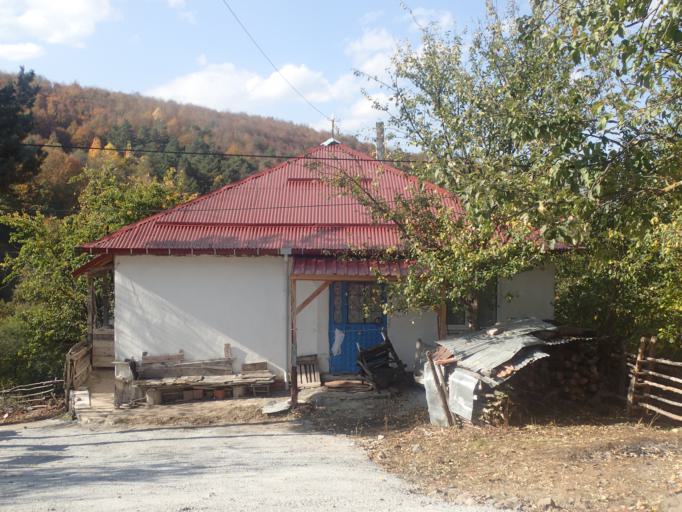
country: TR
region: Ordu
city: Topcam
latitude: 40.5828
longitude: 37.7044
